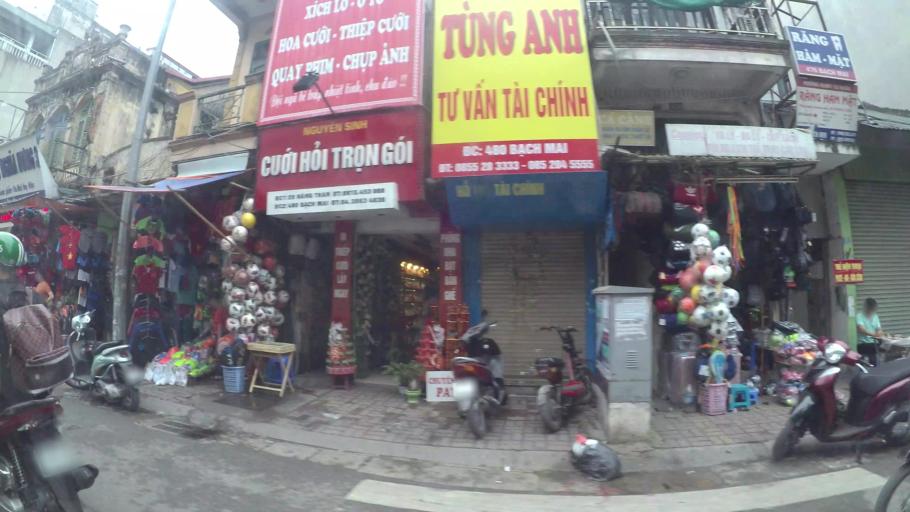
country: VN
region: Ha Noi
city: Hai BaTrung
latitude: 20.9976
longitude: 105.8501
